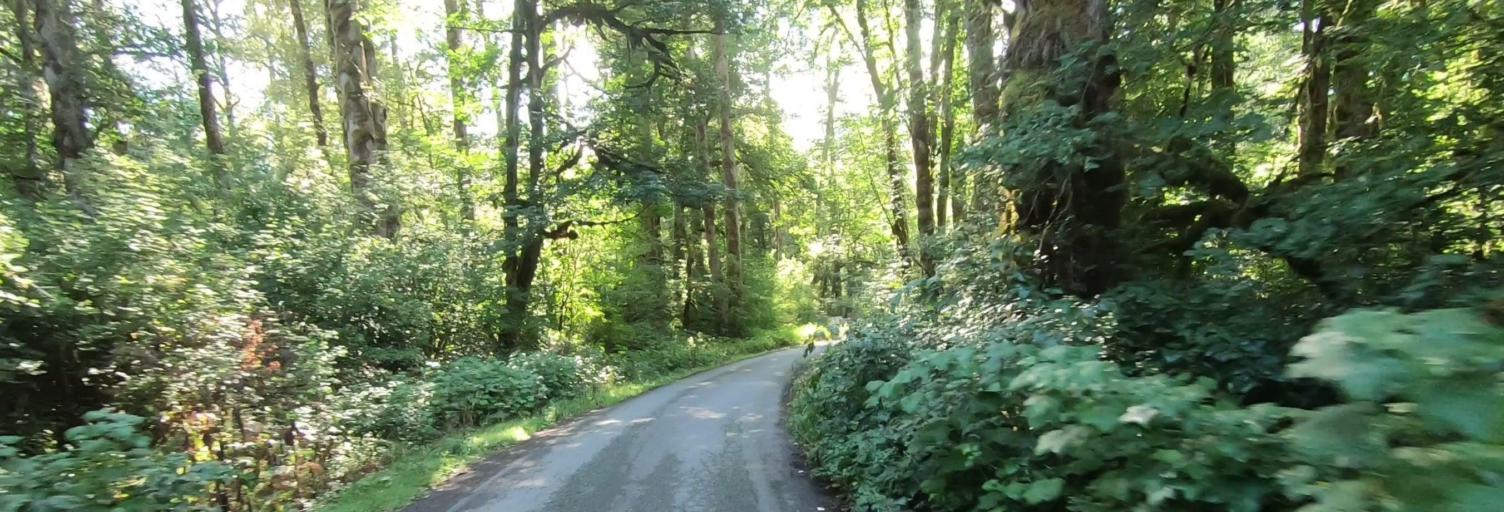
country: US
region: Washington
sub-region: Whatcom County
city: Peaceful Valley
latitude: 48.9019
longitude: -121.9342
